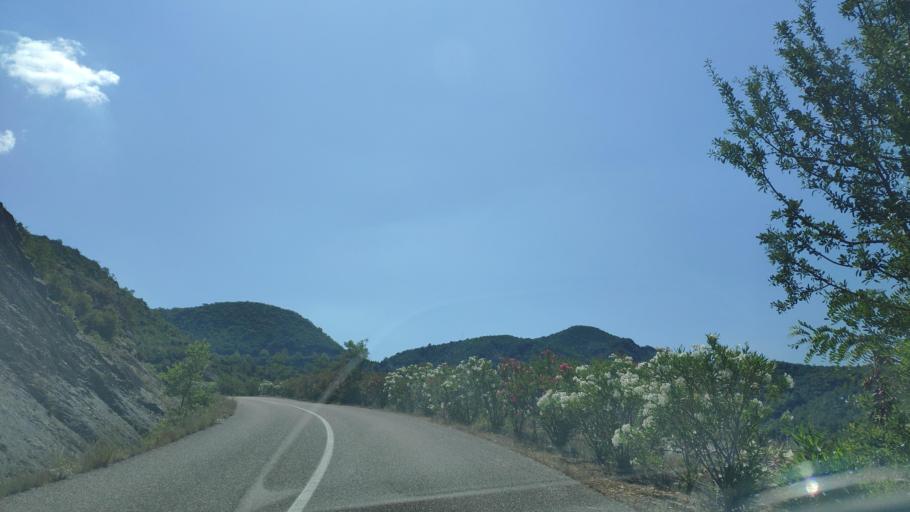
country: GR
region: Central Greece
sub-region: Nomos Evrytanias
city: Kerasochori
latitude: 39.0072
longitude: 21.5266
